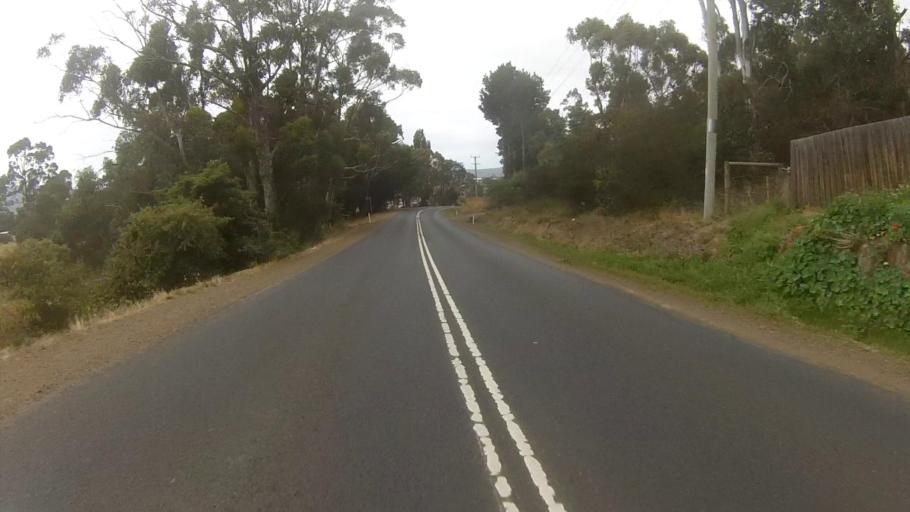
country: AU
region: Tasmania
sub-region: Kingborough
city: Margate
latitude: -43.0178
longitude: 147.2528
